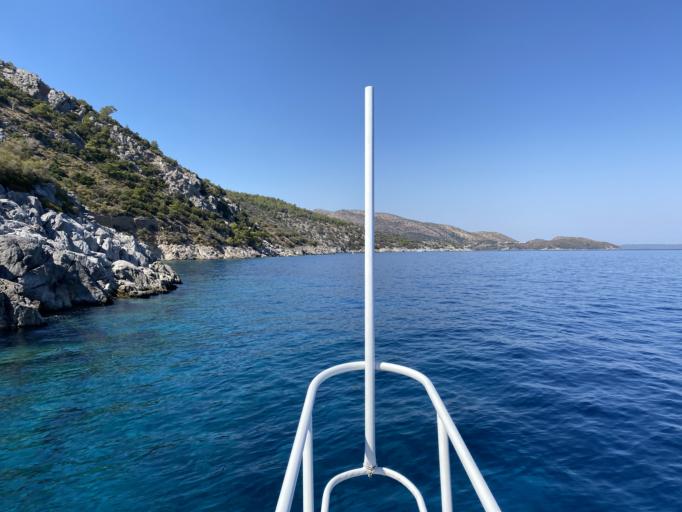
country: TR
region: Mugla
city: Datca
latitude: 36.6746
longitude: 27.6736
